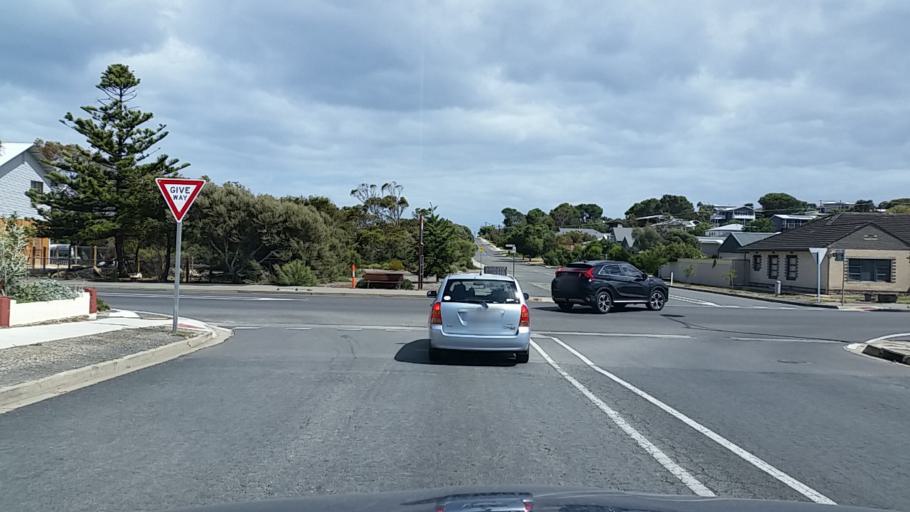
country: AU
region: South Australia
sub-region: Alexandrina
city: Port Elliot
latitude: -35.5306
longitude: 138.6769
